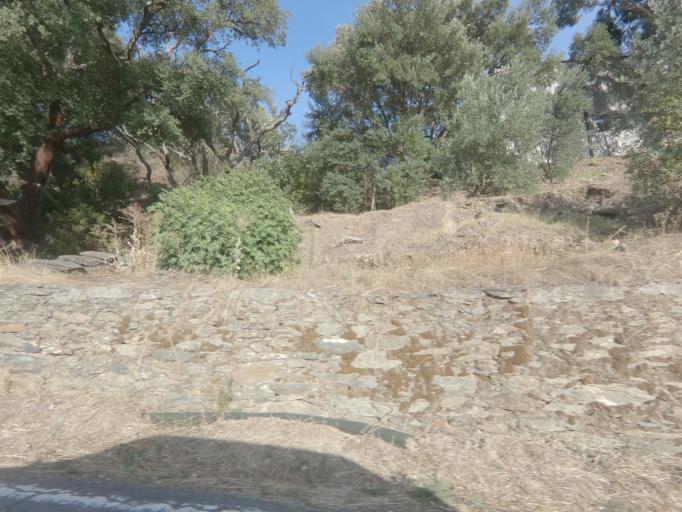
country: PT
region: Vila Real
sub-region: Sabrosa
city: Vilela
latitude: 41.2099
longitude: -7.5406
